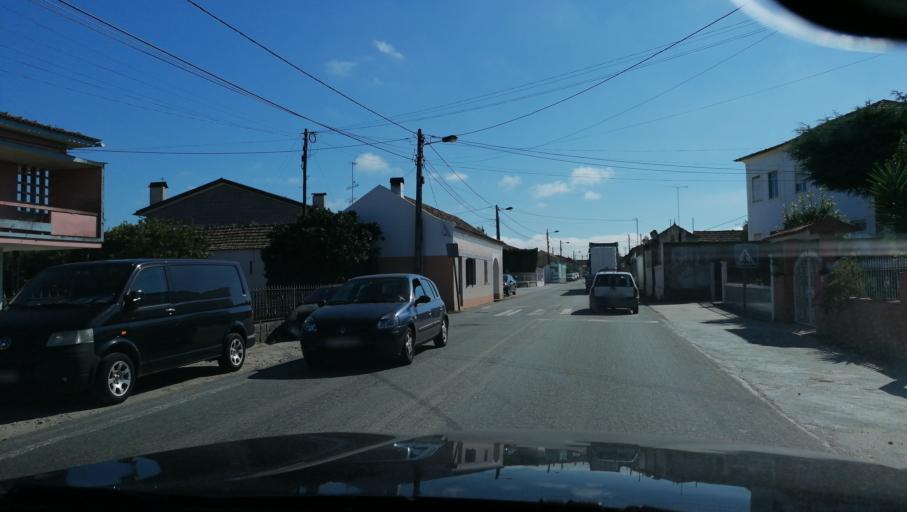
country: PT
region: Aveiro
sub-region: Aveiro
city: Aveiro
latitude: 40.6775
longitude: -8.5988
